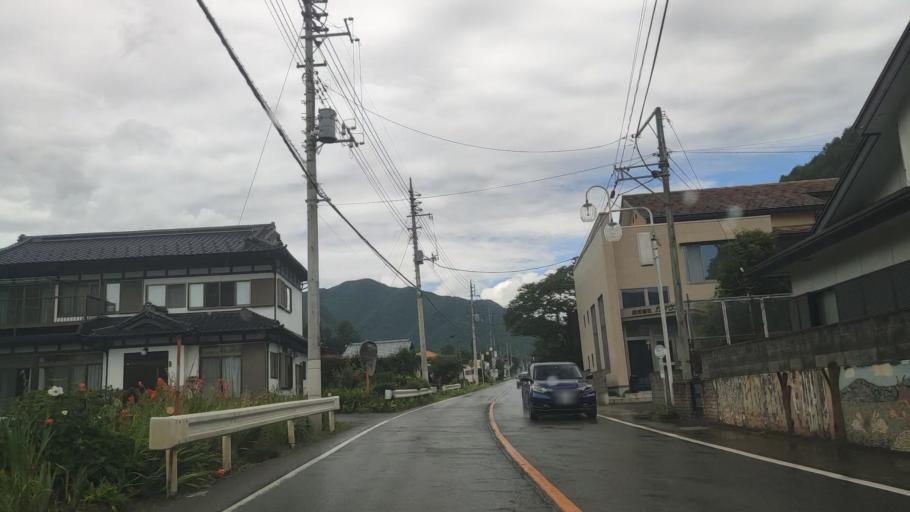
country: JP
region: Gunma
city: Numata
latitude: 36.7552
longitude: 139.2296
